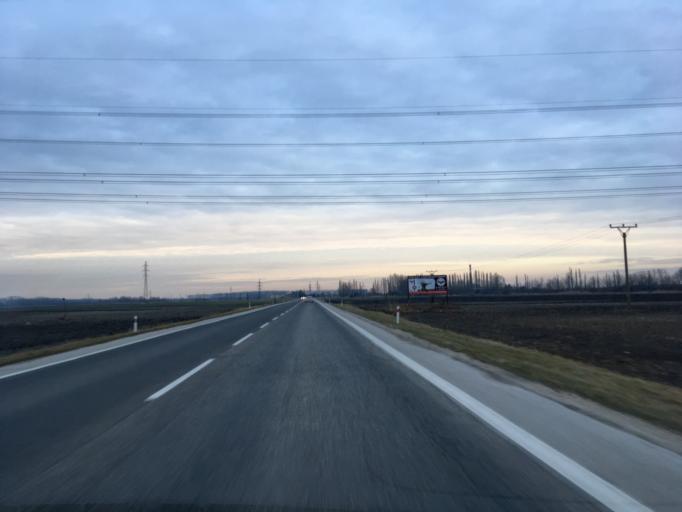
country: SK
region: Trnavsky
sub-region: Okres Dunajska Streda
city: Velky Meder
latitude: 47.8848
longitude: 17.7470
